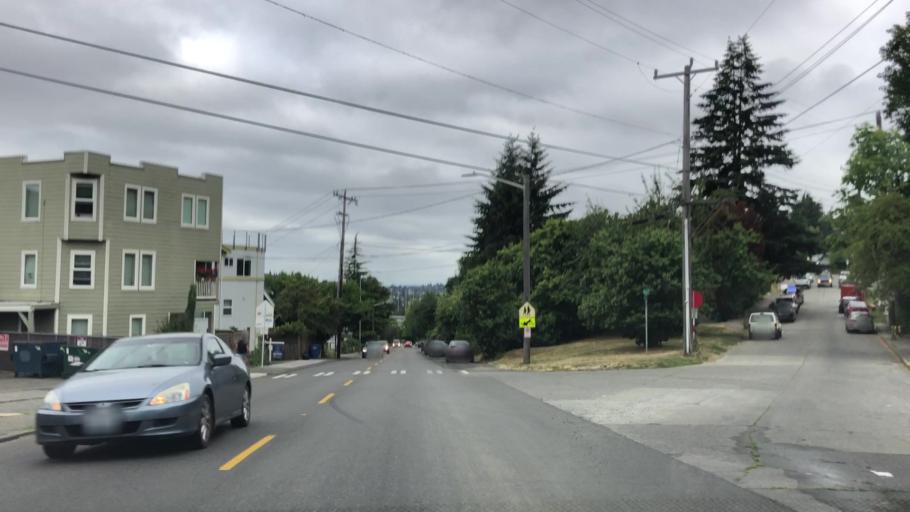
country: US
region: Washington
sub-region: King County
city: Seattle
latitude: 47.6379
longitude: -122.3726
